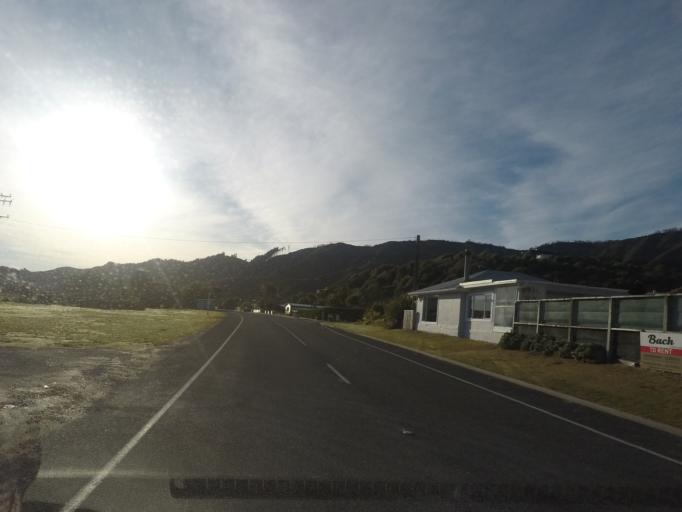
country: NZ
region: Tasman
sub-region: Tasman District
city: Takaka
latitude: -40.8229
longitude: 172.9077
